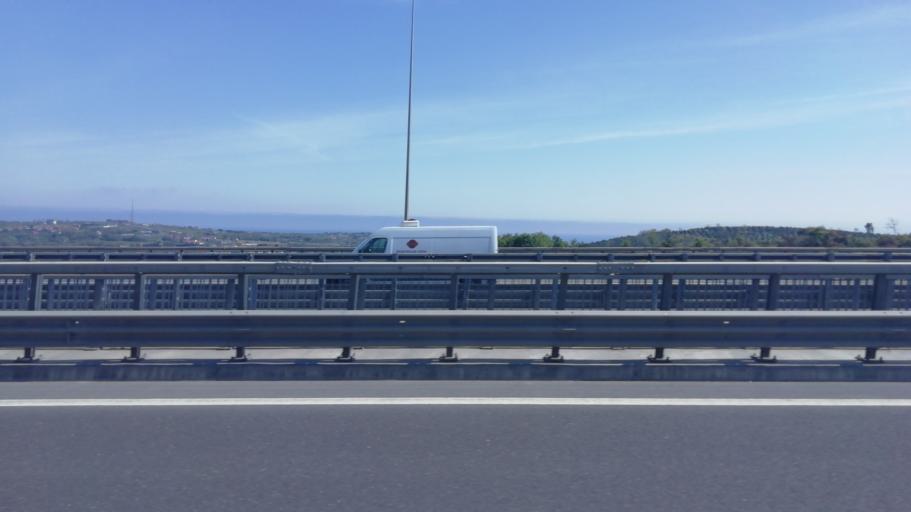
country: TR
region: Istanbul
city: Arikoey
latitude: 41.2269
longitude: 28.9804
